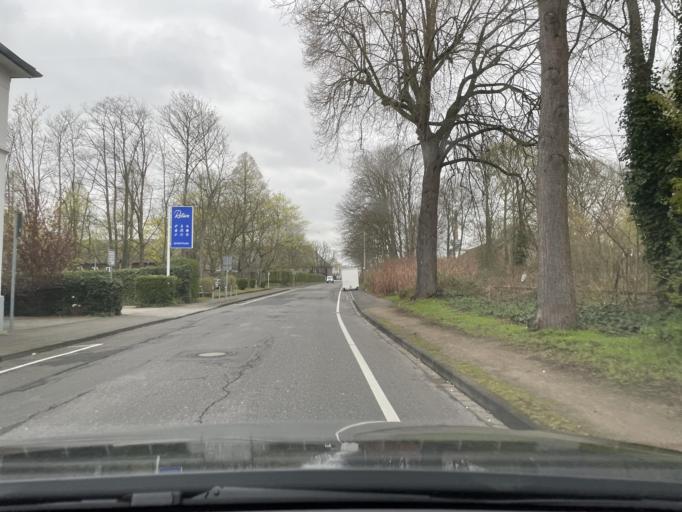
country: DE
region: North Rhine-Westphalia
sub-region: Regierungsbezirk Dusseldorf
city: Monchengladbach
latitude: 51.1799
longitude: 6.4490
